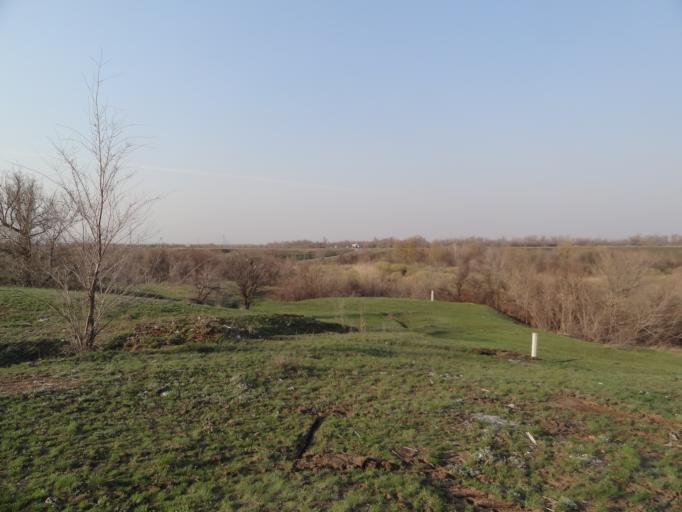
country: RU
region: Saratov
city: Privolzhskiy
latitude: 51.3313
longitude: 46.0374
